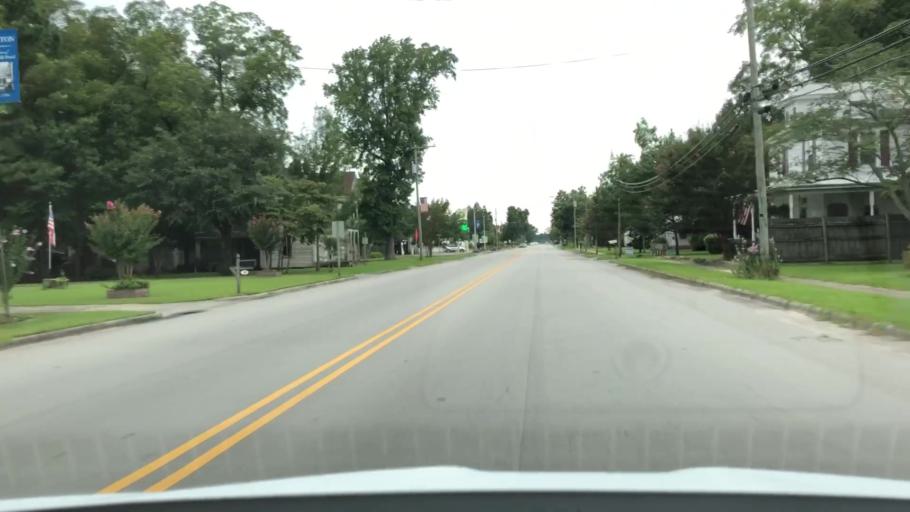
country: US
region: North Carolina
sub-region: Jones County
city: Trenton
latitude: 35.0654
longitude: -77.3590
